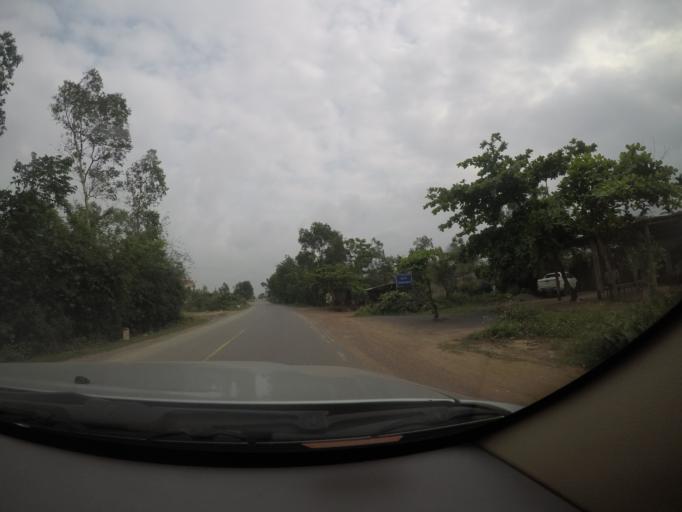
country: VN
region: Quang Binh
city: Quan Hau
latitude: 17.4180
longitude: 106.5968
